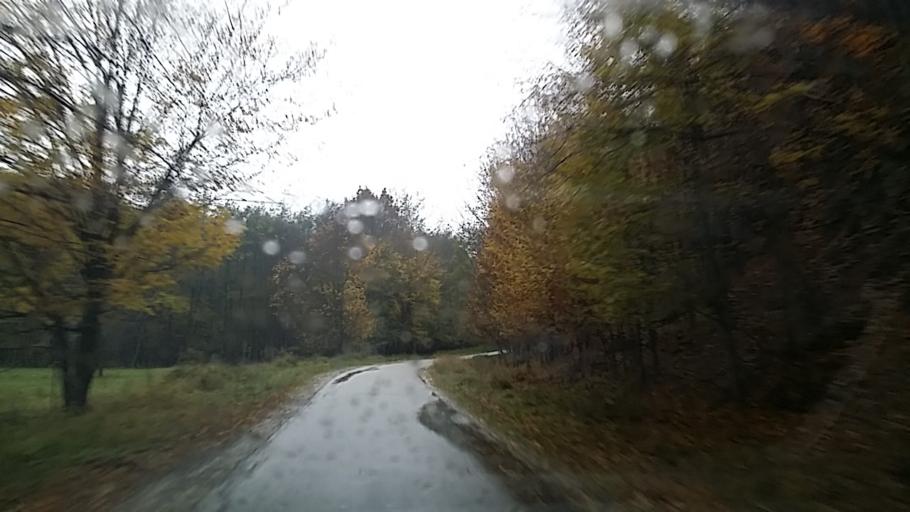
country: HU
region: Borsod-Abauj-Zemplen
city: Tolcsva
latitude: 48.4332
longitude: 21.4575
